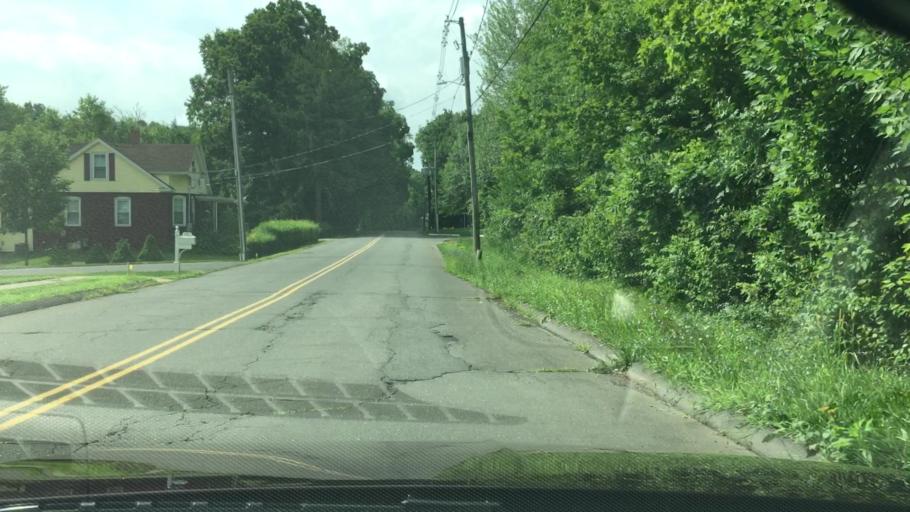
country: US
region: Connecticut
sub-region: Hartford County
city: Kensington
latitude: 41.6224
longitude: -72.7666
